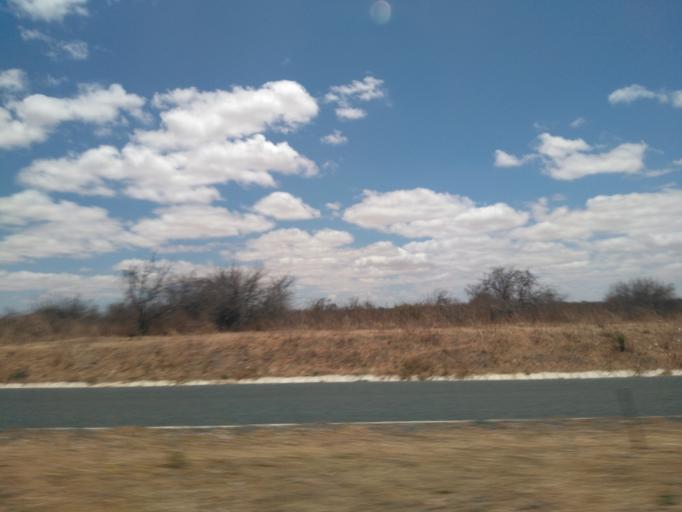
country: TZ
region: Dodoma
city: Kisasa
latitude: -6.1690
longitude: 35.8459
